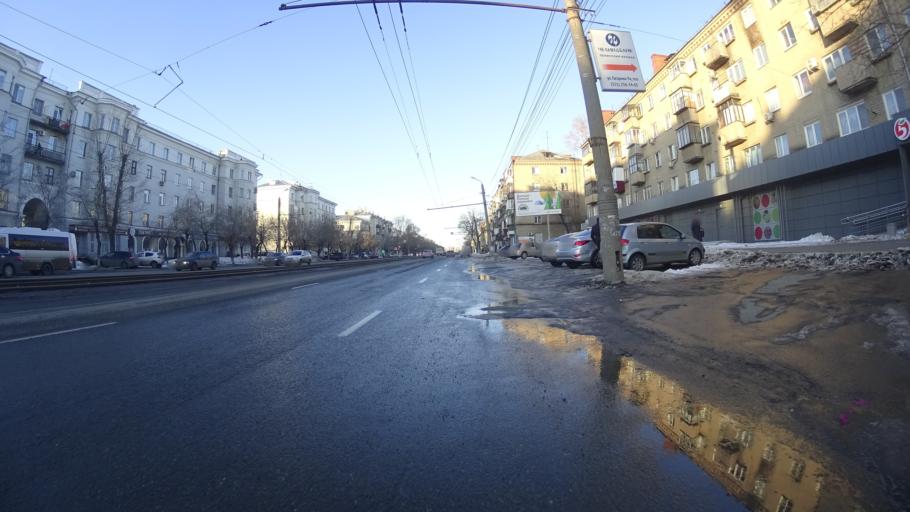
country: RU
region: Chelyabinsk
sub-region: Gorod Chelyabinsk
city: Chelyabinsk
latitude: 55.1401
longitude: 61.4418
